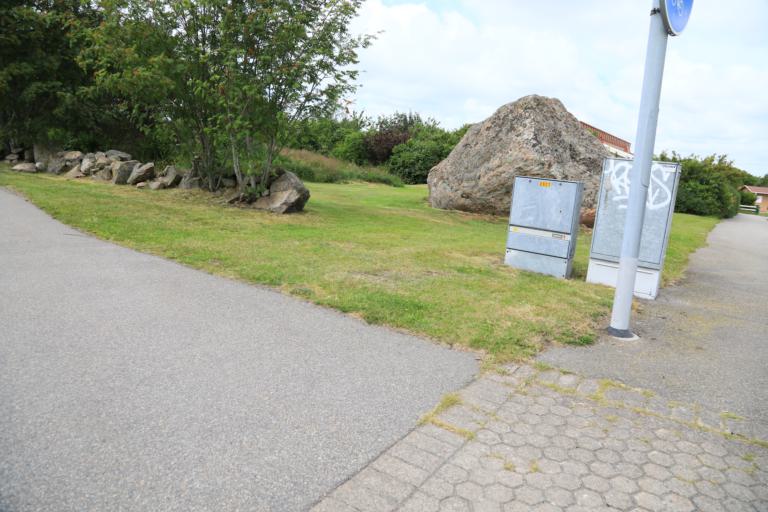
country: SE
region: Halland
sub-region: Varbergs Kommun
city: Traslovslage
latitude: 57.1117
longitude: 12.3010
